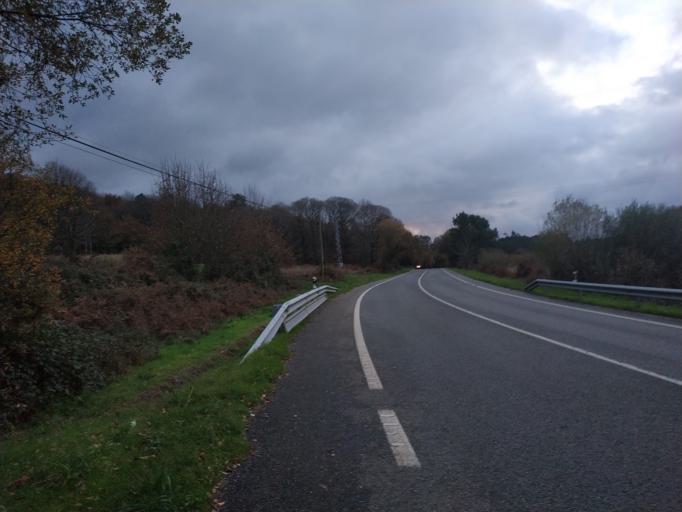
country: ES
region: Galicia
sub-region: Provincia de Pontevedra
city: Silleda
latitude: 42.7804
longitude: -8.1721
